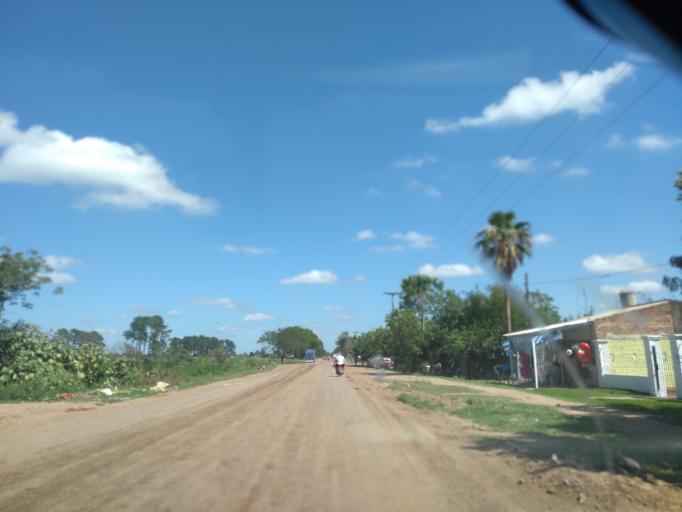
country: AR
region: Chaco
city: Fontana
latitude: -27.4095
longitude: -59.0333
